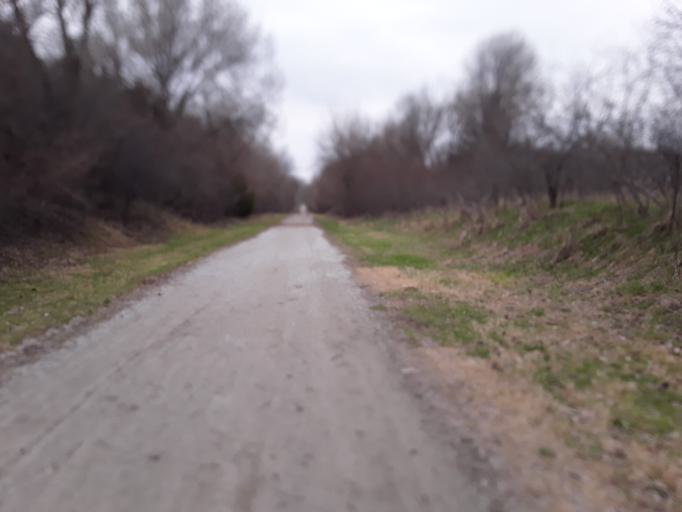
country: US
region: Nebraska
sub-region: Lancaster County
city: Lincoln
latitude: 40.8514
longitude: -96.6164
